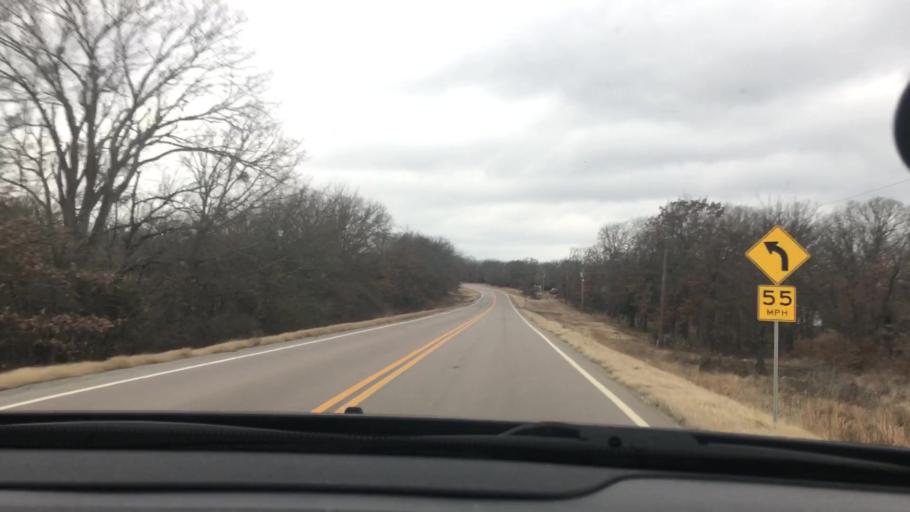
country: US
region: Oklahoma
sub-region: Coal County
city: Coalgate
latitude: 34.3743
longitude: -96.3672
